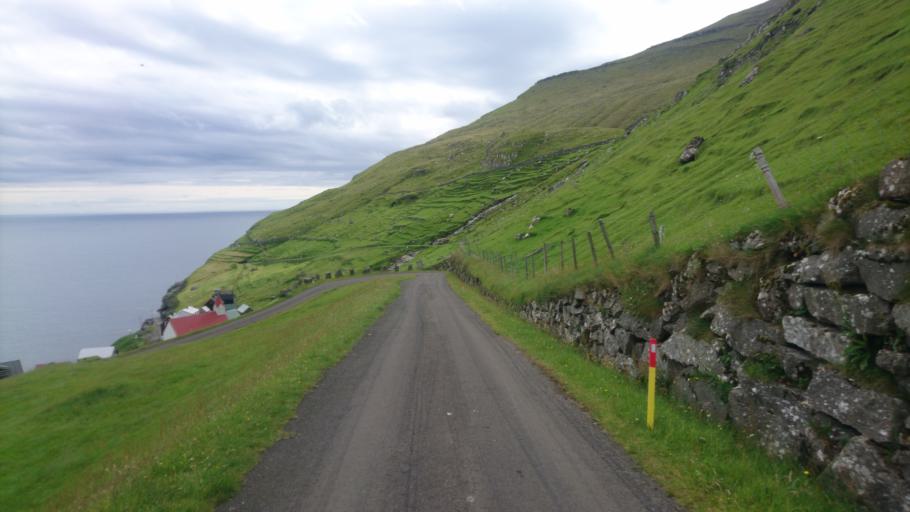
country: FO
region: Nordoyar
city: Klaksvik
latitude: 62.3306
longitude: -6.2779
